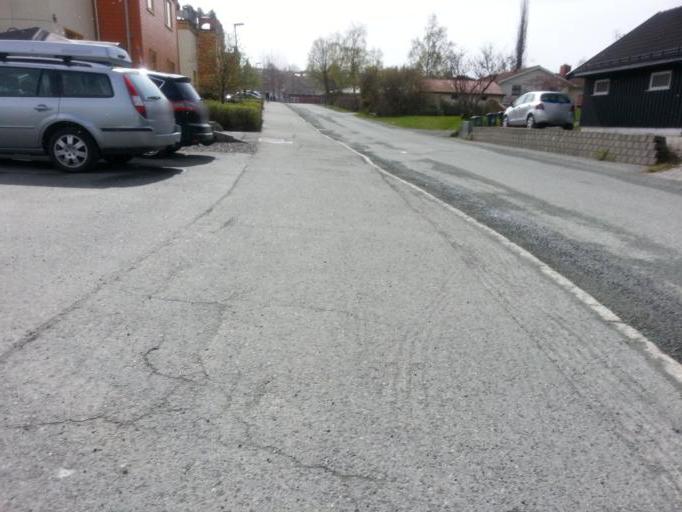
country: NO
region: Sor-Trondelag
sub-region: Trondheim
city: Trondheim
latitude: 63.3961
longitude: 10.3460
